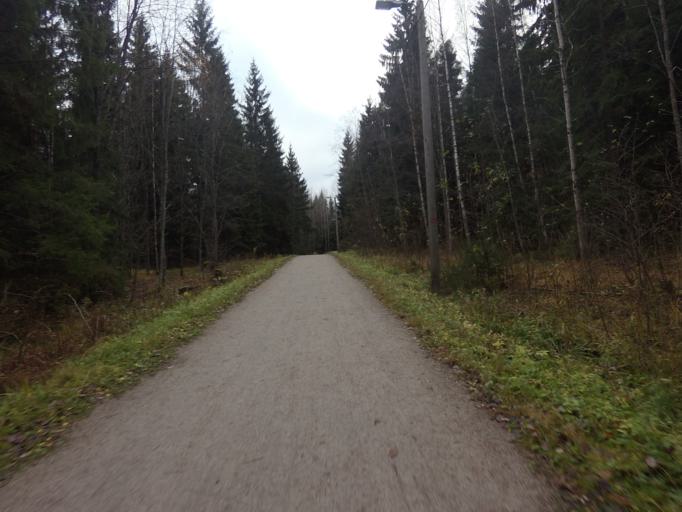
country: FI
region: Uusimaa
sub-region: Helsinki
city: Kauniainen
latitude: 60.1929
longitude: 24.6980
